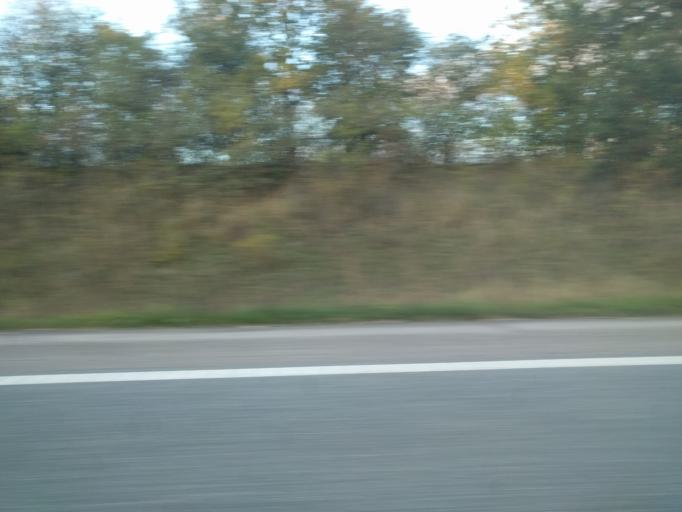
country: DK
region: South Denmark
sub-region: Nyborg Kommune
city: Nyborg
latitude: 55.3369
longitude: 10.7319
